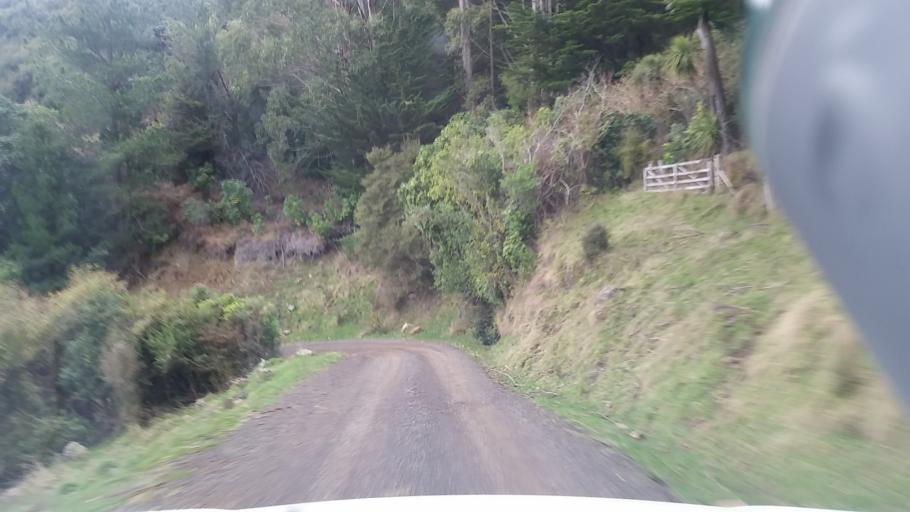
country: NZ
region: Canterbury
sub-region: Christchurch City
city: Christchurch
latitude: -43.8240
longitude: 172.9900
